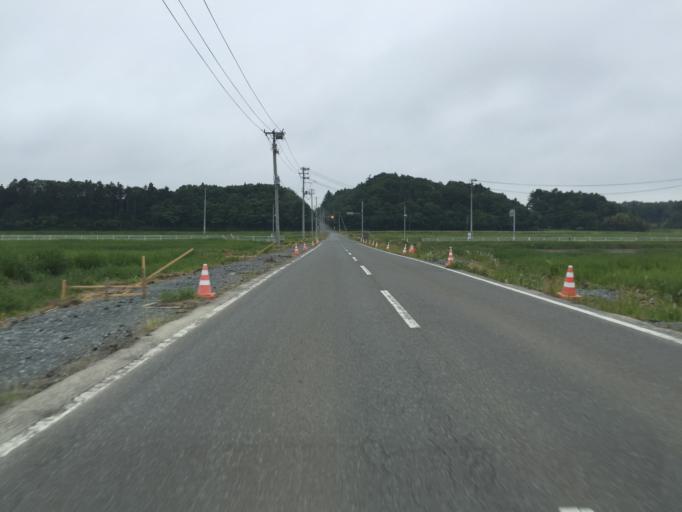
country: JP
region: Fukushima
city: Namie
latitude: 37.6805
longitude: 141.0040
